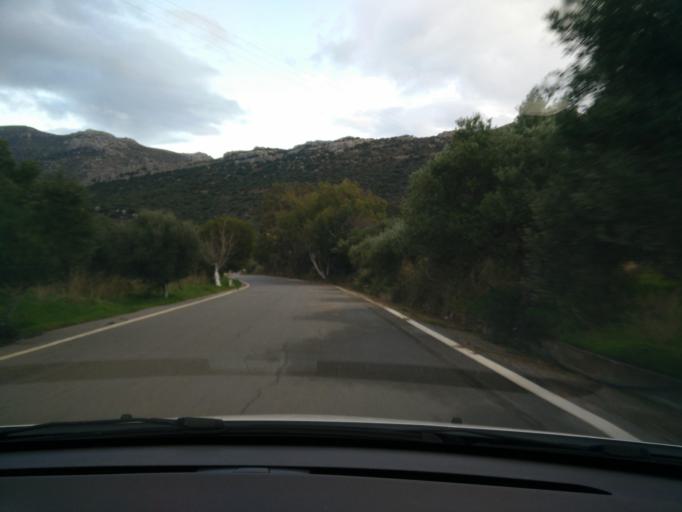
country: GR
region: Crete
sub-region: Nomos Lasithiou
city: Gra Liyia
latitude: 35.0836
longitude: 25.7089
